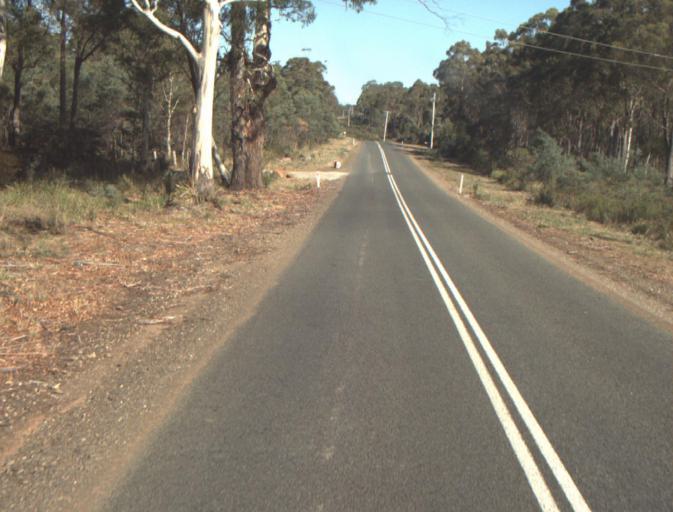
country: AU
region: Tasmania
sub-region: Launceston
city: Mayfield
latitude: -41.3016
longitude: 147.1334
